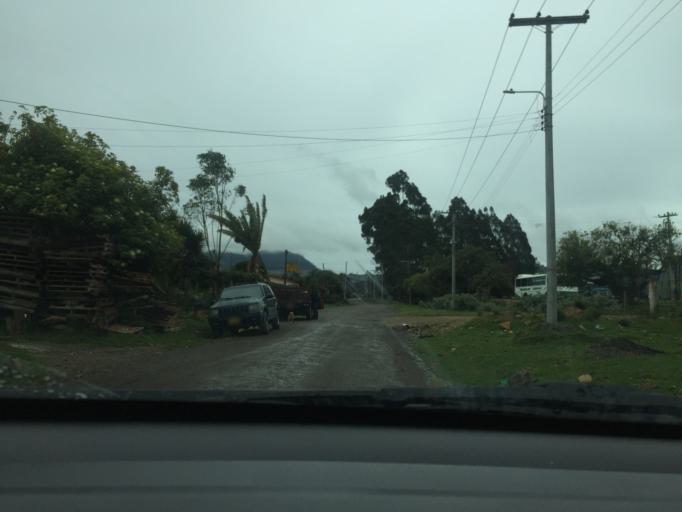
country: CO
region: Cundinamarca
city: El Rosal
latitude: 4.8276
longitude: -74.2874
